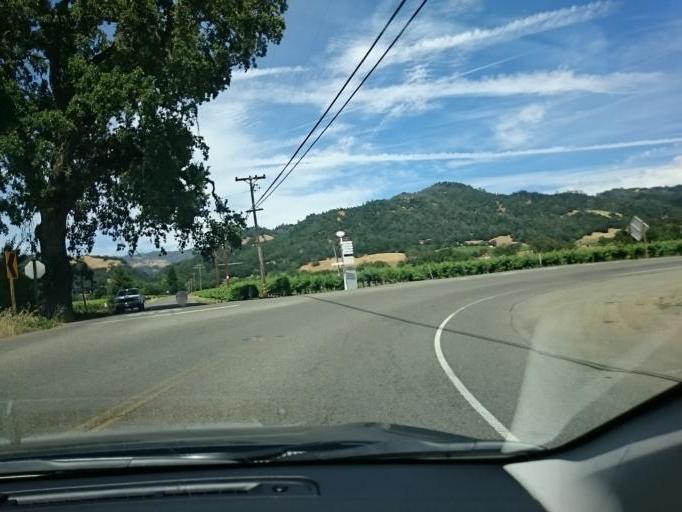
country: US
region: California
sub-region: Sonoma County
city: Healdsburg
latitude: 38.6715
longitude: -122.8134
